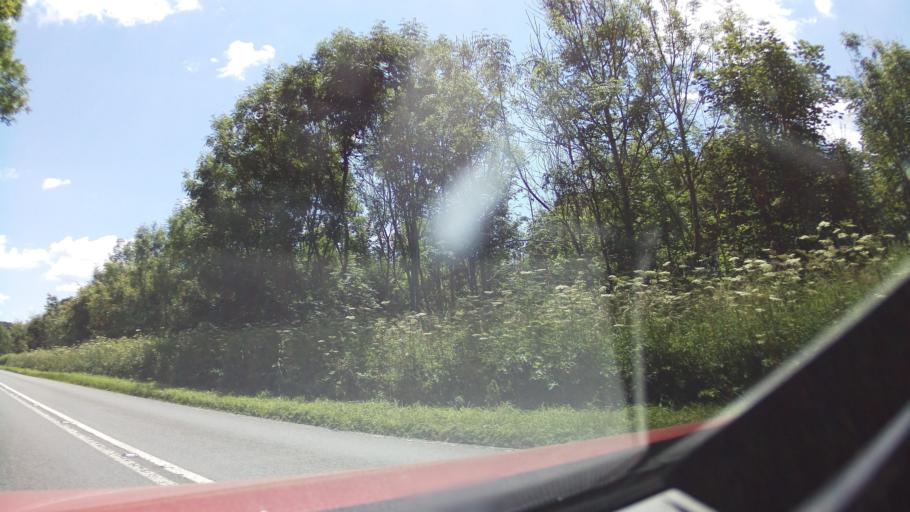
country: GB
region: England
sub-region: Derbyshire
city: Bakewell
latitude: 53.1420
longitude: -1.7570
